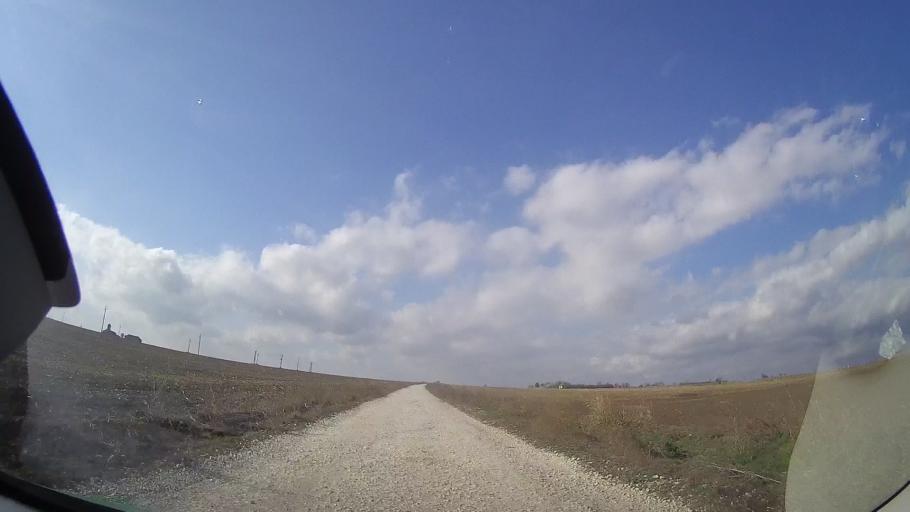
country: RO
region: Constanta
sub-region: Comuna Douazeci si Trei August
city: Douazeci si Trei August
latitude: 43.9103
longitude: 28.6017
